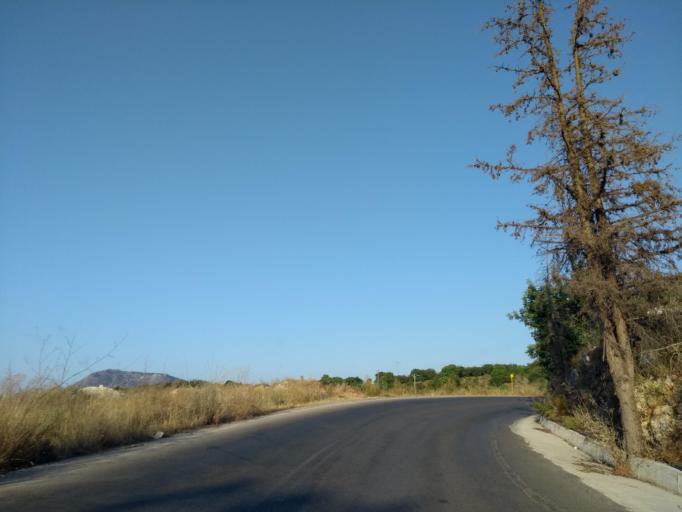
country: GR
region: Crete
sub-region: Nomos Chanias
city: Kalivai
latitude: 35.4282
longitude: 24.1800
